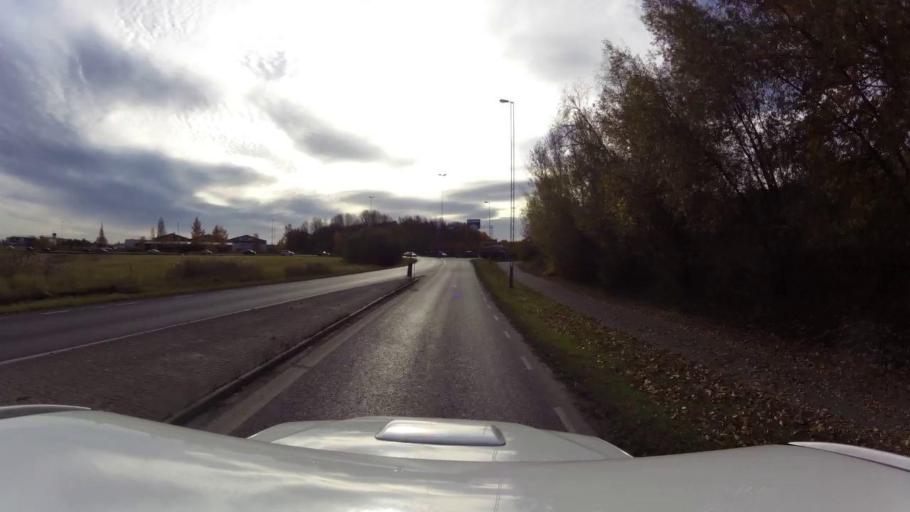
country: SE
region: OEstergoetland
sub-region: Linkopings Kommun
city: Linkoping
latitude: 58.4244
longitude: 15.6376
